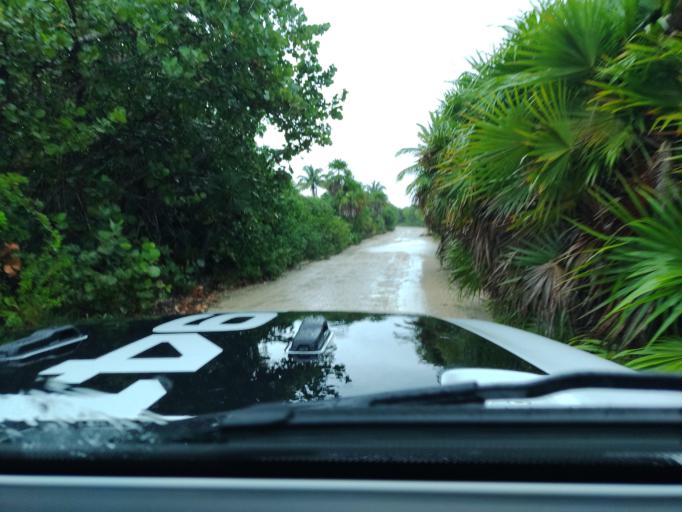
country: MX
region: Quintana Roo
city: Tulum
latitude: 19.9302
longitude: -87.4511
